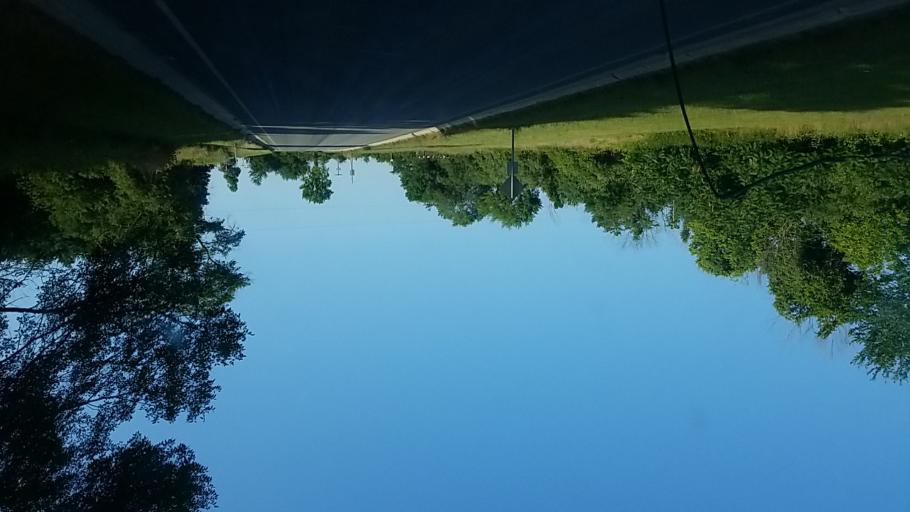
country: US
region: Michigan
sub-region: Newaygo County
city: Fremont
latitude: 43.3508
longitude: -85.9414
